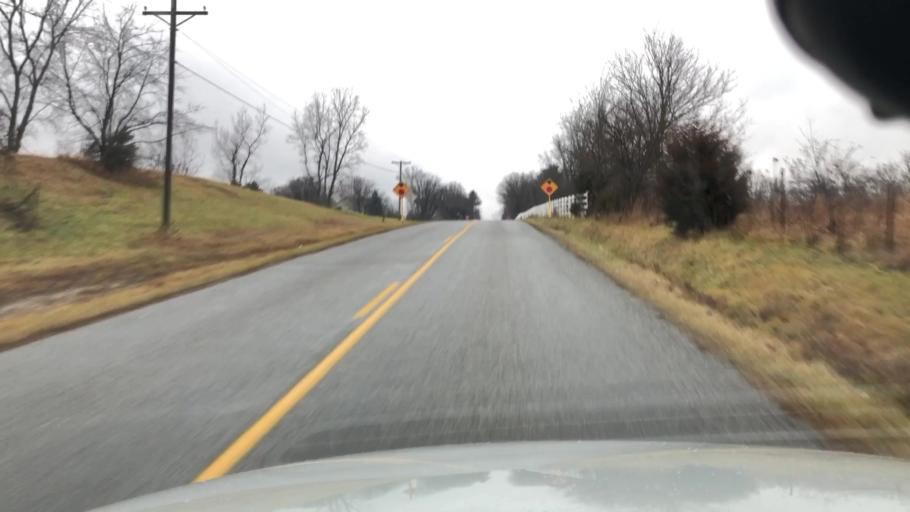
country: US
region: Ohio
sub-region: Allen County
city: Lima
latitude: 40.7690
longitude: -84.0131
